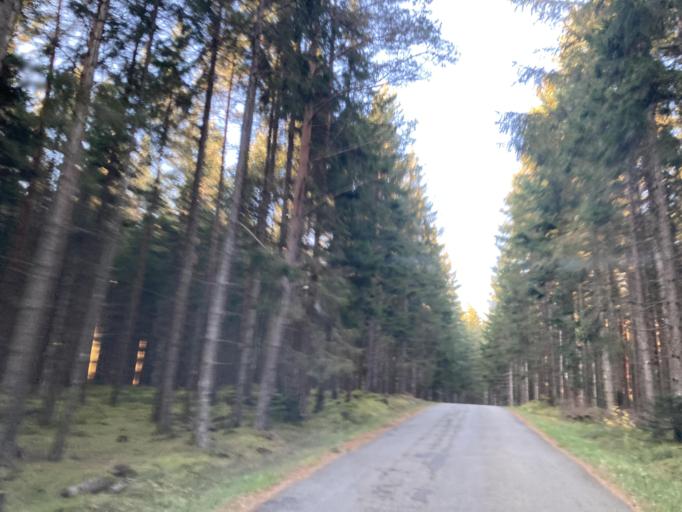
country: DE
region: Baden-Wuerttemberg
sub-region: Freiburg Region
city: Braunlingen
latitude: 47.9877
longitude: 8.3887
